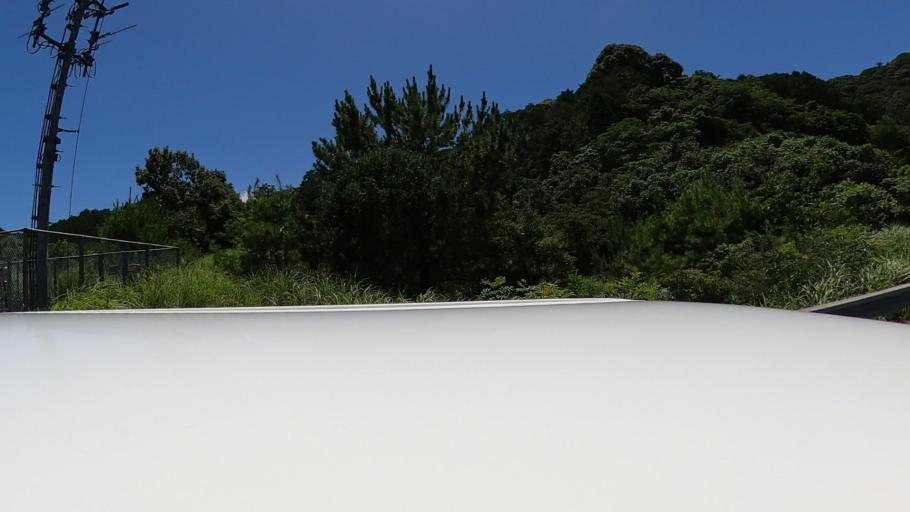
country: JP
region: Miyazaki
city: Nobeoka
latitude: 32.5454
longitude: 131.6469
